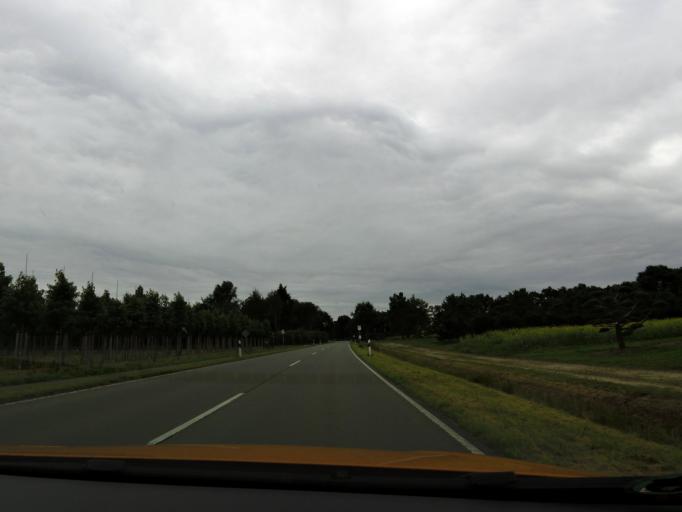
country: DE
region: Lower Saxony
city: Bad Zwischenahn
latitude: 53.2389
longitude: 7.9871
